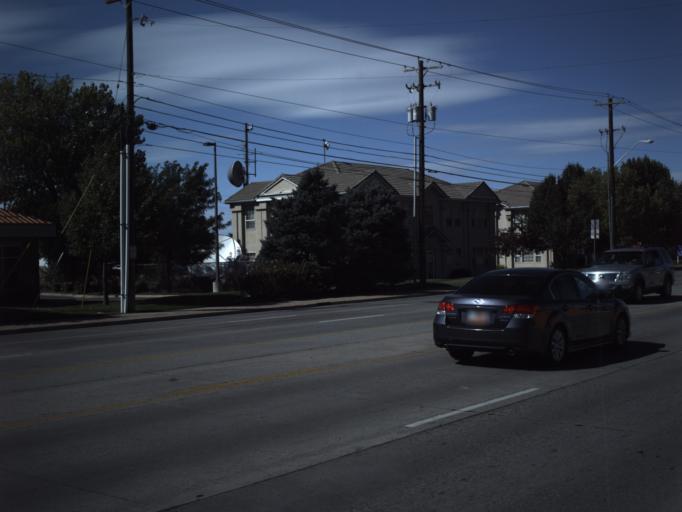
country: US
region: Utah
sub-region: Salt Lake County
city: Taylorsville
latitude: 40.7116
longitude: -111.9388
